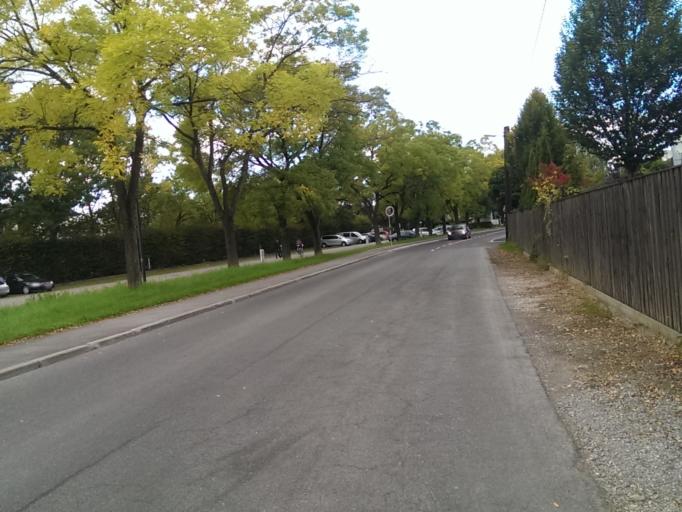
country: AT
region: Styria
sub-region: Graz Stadt
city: Graz
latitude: 47.0545
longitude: 15.4678
